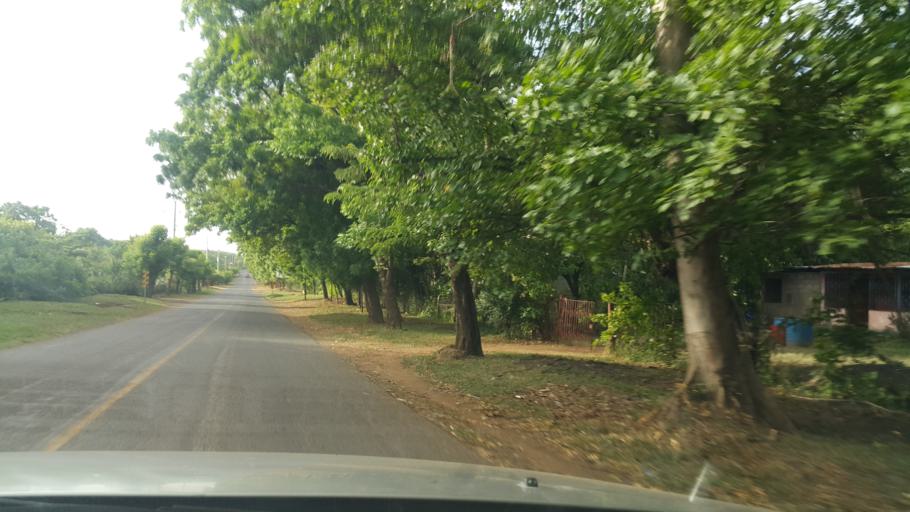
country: NI
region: Managua
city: San Rafael del Sur
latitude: 11.8211
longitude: -86.4751
